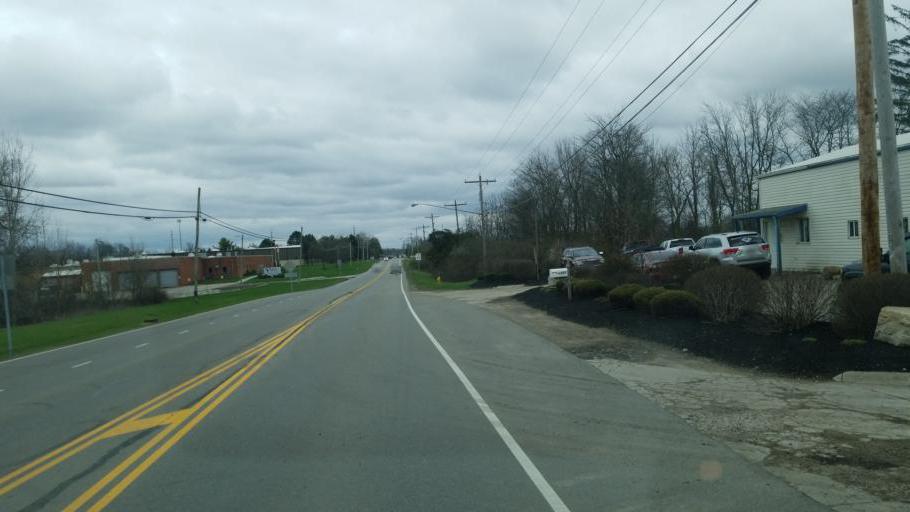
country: US
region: Ohio
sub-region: Delaware County
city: Delaware
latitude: 40.2824
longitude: -83.0910
